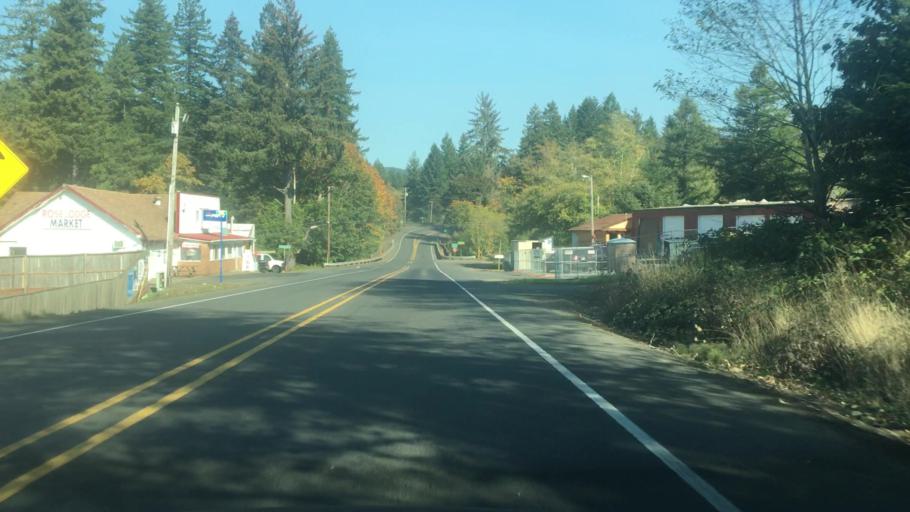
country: US
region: Oregon
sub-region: Lincoln County
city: Rose Lodge
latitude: 45.0098
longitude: -123.8816
